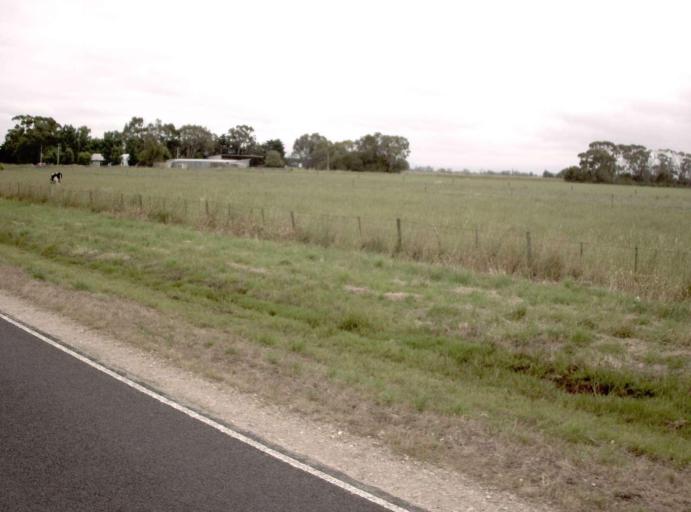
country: AU
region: Victoria
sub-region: Wellington
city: Sale
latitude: -38.0461
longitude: 146.9456
